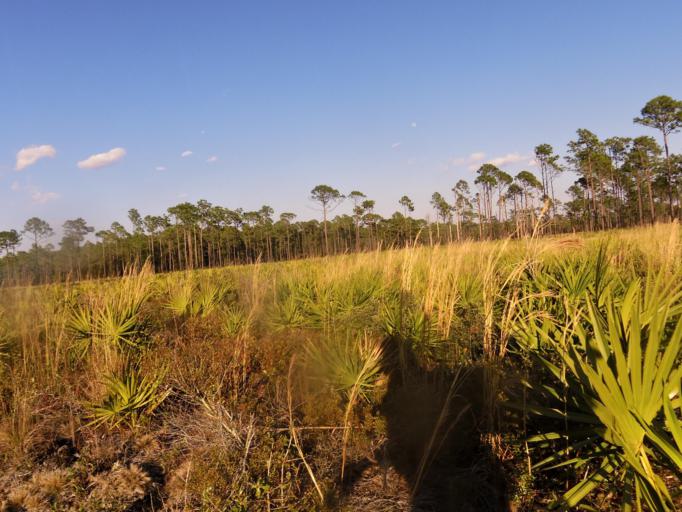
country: US
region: Florida
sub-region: Duval County
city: Atlantic Beach
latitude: 30.4748
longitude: -81.4994
